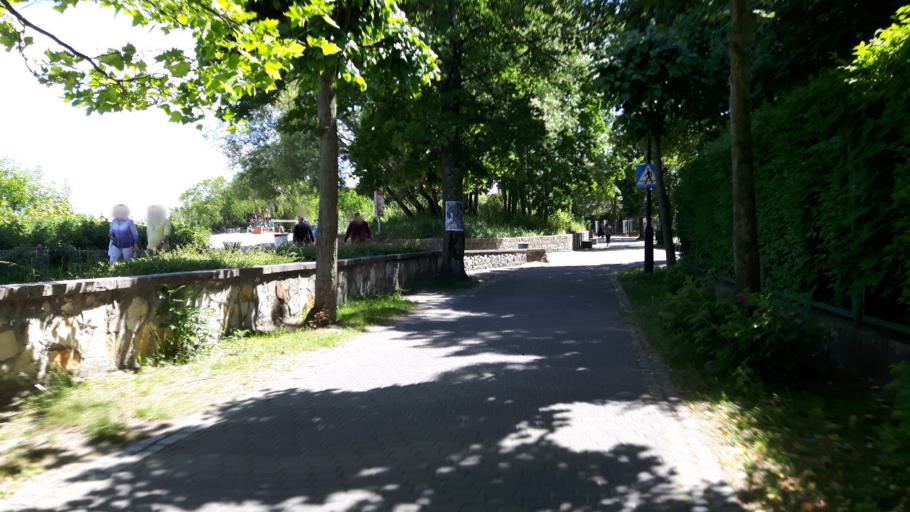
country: PL
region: Pomeranian Voivodeship
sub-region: Sopot
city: Sopot
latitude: 54.4383
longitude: 18.5786
